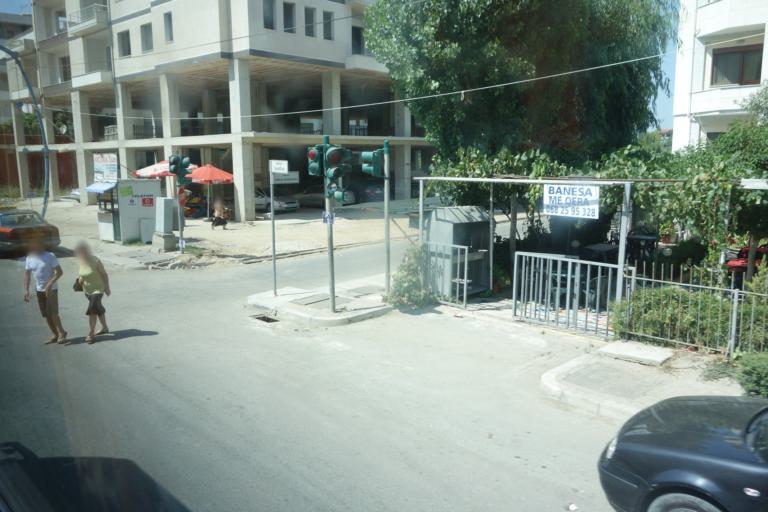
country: AL
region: Durres
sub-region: Rrethi i Durresit
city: Rrashbull
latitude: 41.3143
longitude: 19.4760
